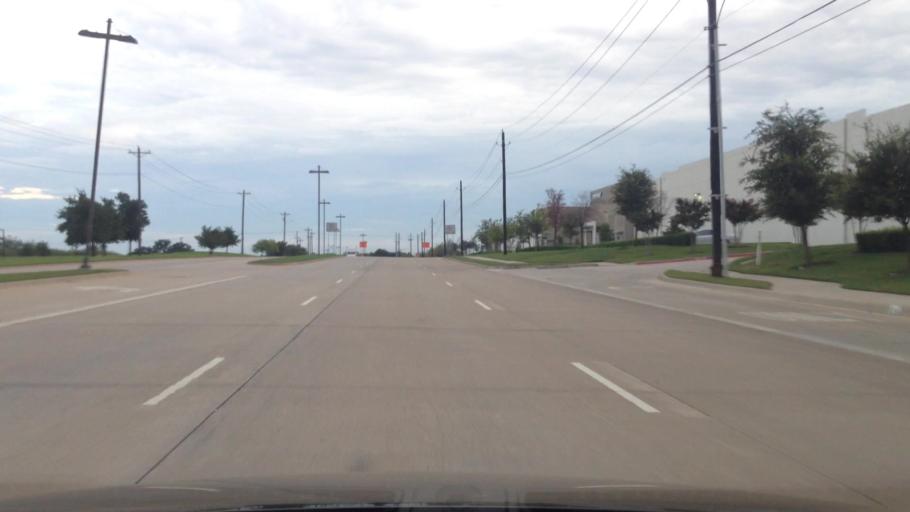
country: US
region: Texas
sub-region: Dallas County
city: Coppell
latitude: 32.9938
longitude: -97.0457
